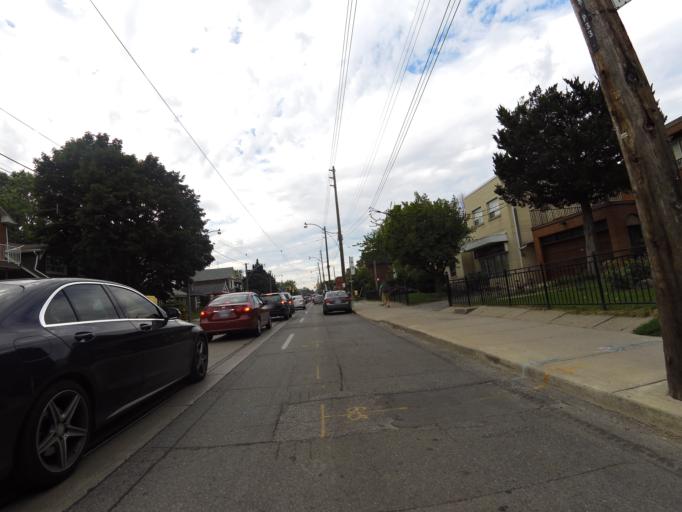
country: CA
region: Ontario
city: Toronto
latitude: 43.6675
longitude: -79.3170
